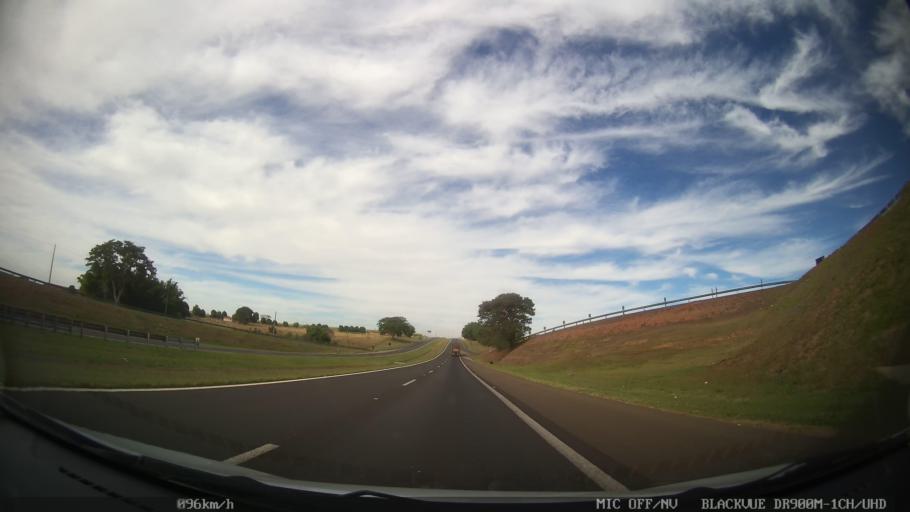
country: BR
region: Sao Paulo
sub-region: Taquaritinga
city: Taquaritinga
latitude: -21.5271
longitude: -48.5241
